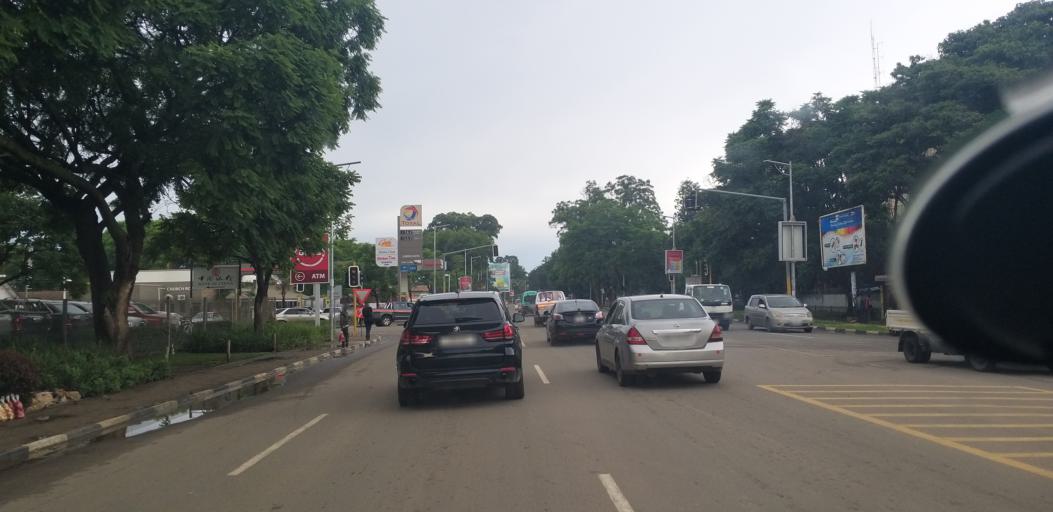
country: ZM
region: Lusaka
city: Lusaka
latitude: -15.4153
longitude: 28.2867
